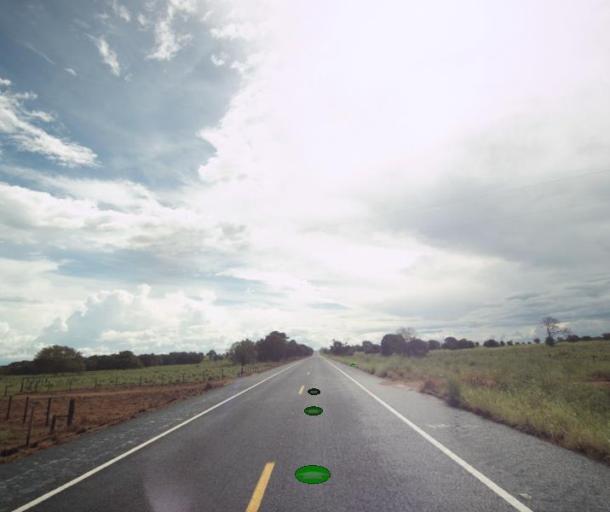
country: BR
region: Goias
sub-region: Sao Miguel Do Araguaia
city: Sao Miguel do Araguaia
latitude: -13.2913
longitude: -50.4135
